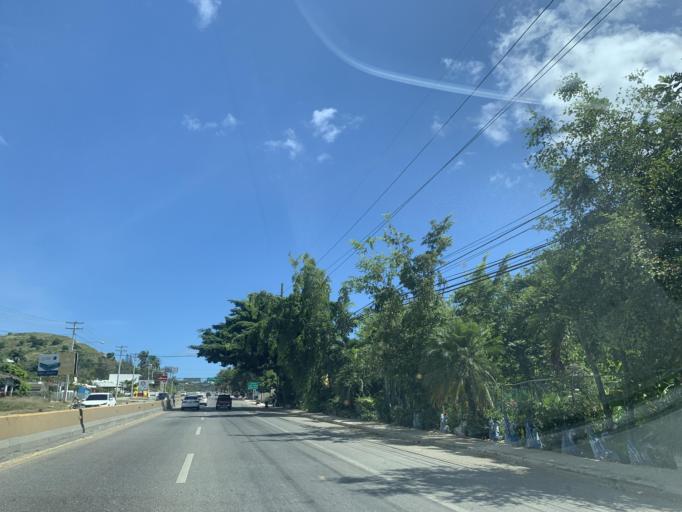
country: DO
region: Puerto Plata
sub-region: Puerto Plata
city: Puerto Plata
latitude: 19.8100
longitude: -70.7301
